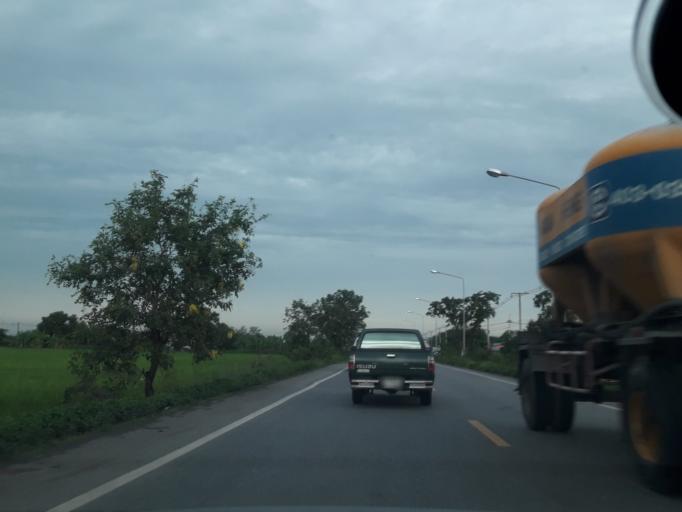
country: TH
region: Phra Nakhon Si Ayutthaya
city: Wang Noi
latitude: 14.1580
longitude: 100.7474
